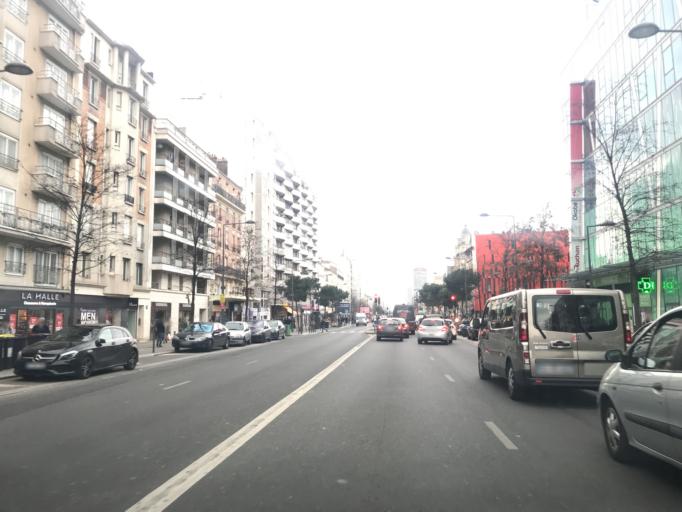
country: FR
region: Ile-de-France
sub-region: Departement du Val-de-Marne
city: Le Kremlin-Bicetre
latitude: 48.8114
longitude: 2.3620
